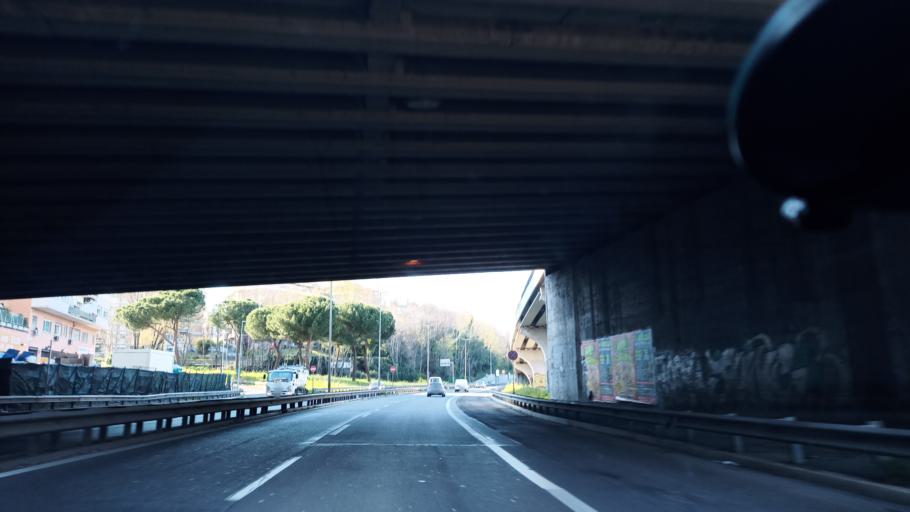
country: IT
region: Latium
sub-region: Citta metropolitana di Roma Capitale
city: Rome
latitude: 41.9336
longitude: 12.5217
